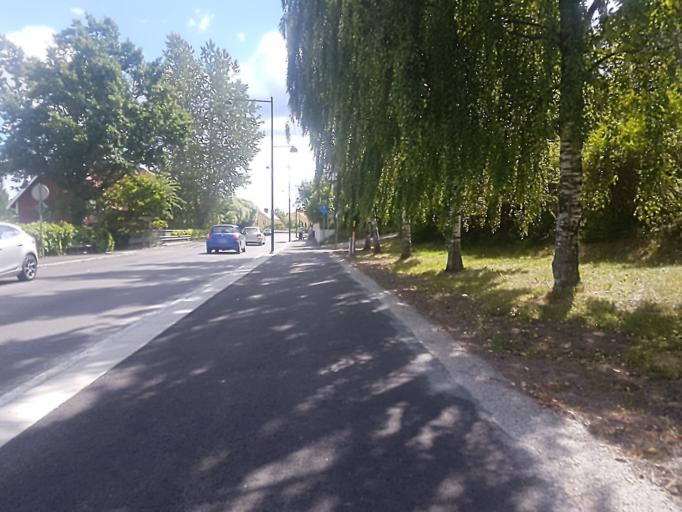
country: SE
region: Soedermanland
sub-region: Gnesta Kommun
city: Gnesta
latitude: 59.0451
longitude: 17.3230
